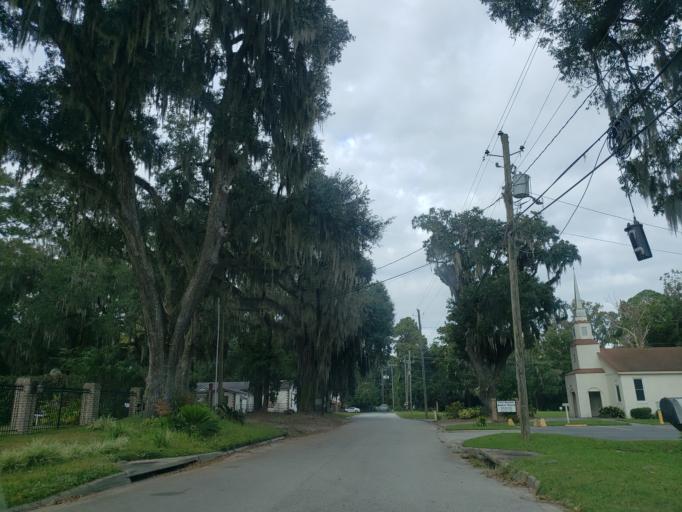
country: US
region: Georgia
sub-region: Chatham County
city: Montgomery
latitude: 31.9441
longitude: -81.1136
